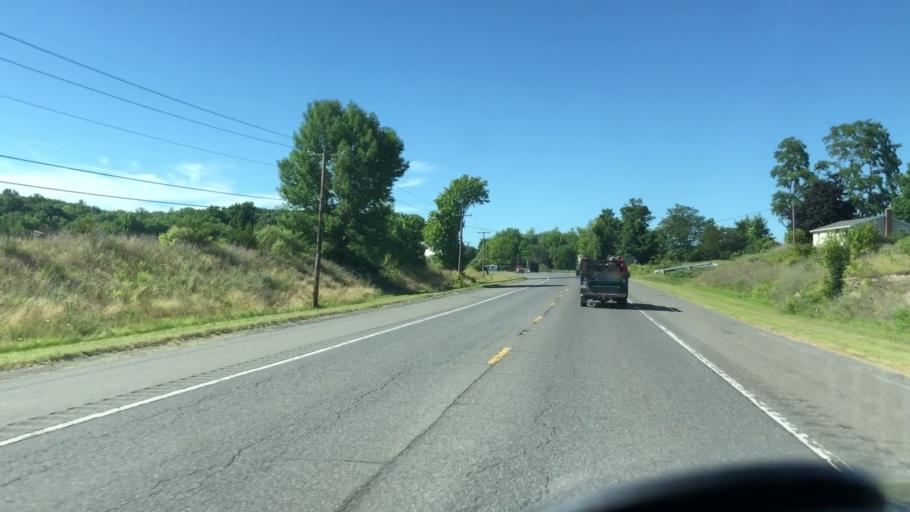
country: US
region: Massachusetts
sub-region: Hampshire County
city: Southampton
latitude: 42.1941
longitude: -72.7261
